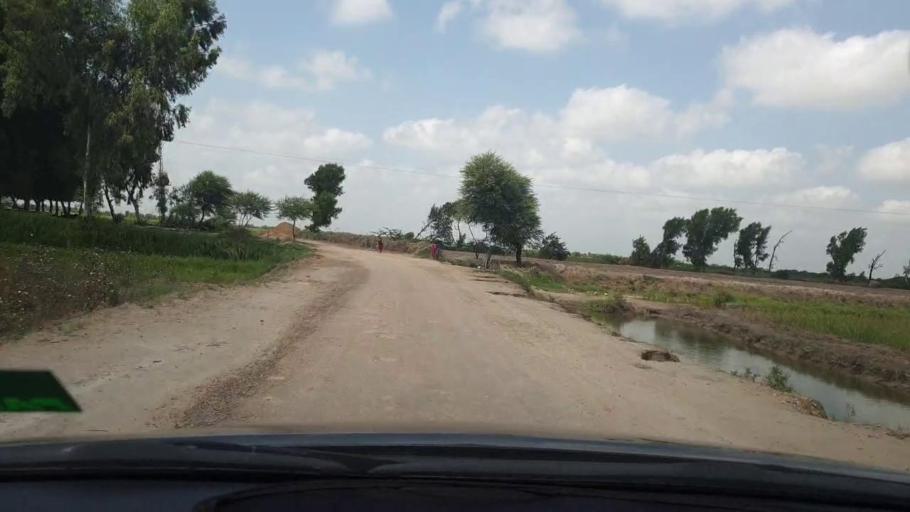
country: PK
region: Sindh
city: Tando Bago
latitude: 24.8723
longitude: 69.0299
